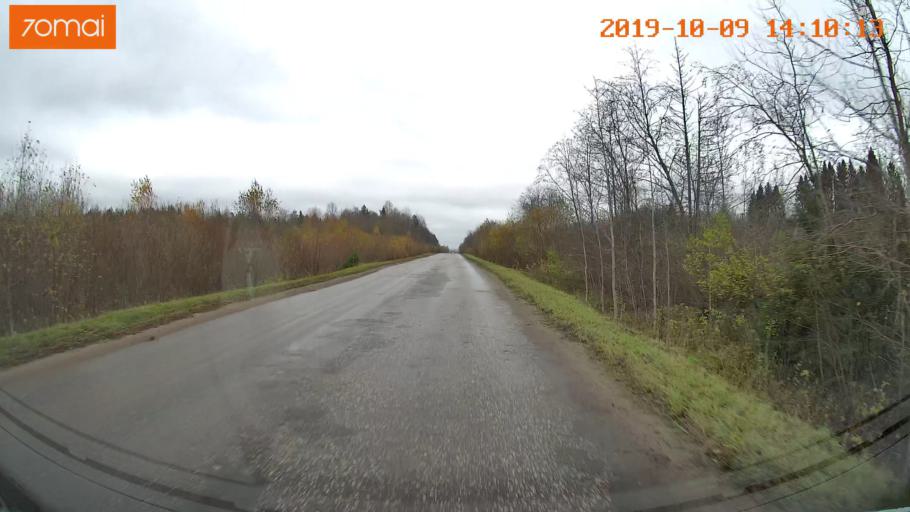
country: RU
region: Kostroma
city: Buy
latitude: 58.4817
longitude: 41.4697
